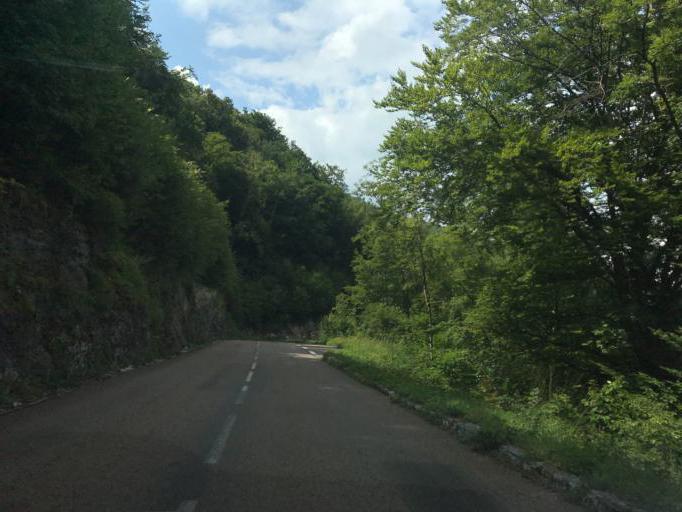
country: FR
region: Franche-Comte
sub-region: Departement du Jura
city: Valfin-les-Saint-Claude
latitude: 46.4161
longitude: 5.8648
